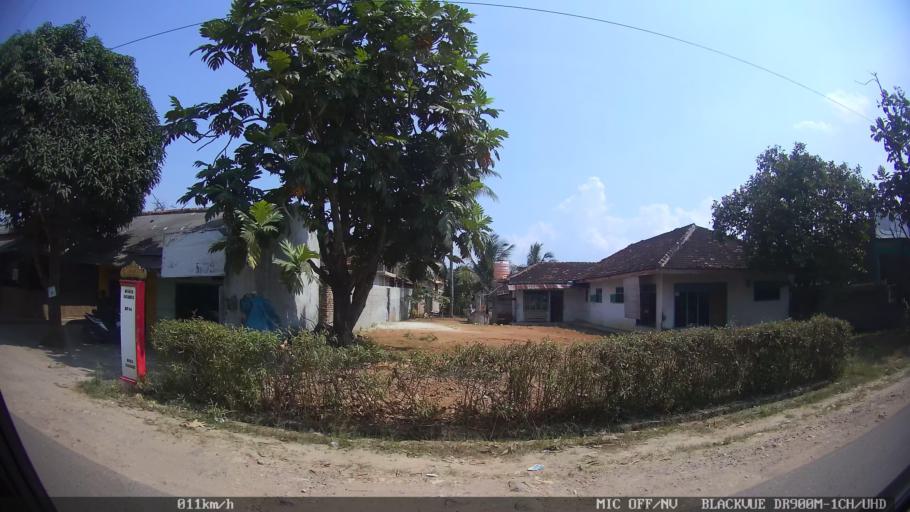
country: ID
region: Lampung
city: Natar
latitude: -5.3074
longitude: 105.2176
